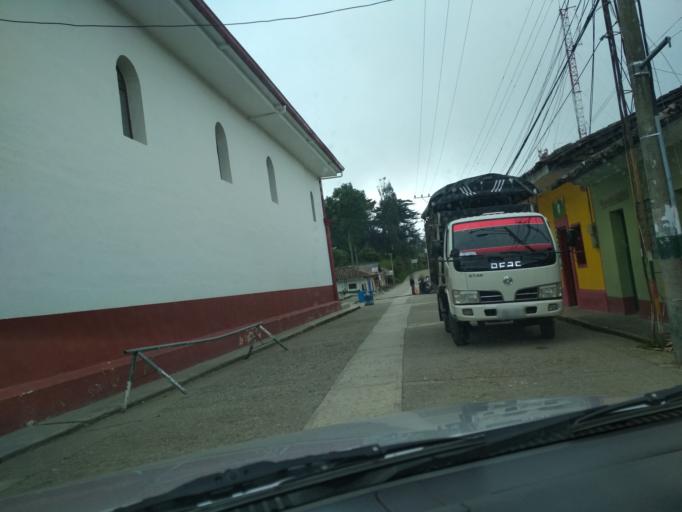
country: CO
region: Cauca
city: Paispamba
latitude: 2.2539
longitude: -76.6143
